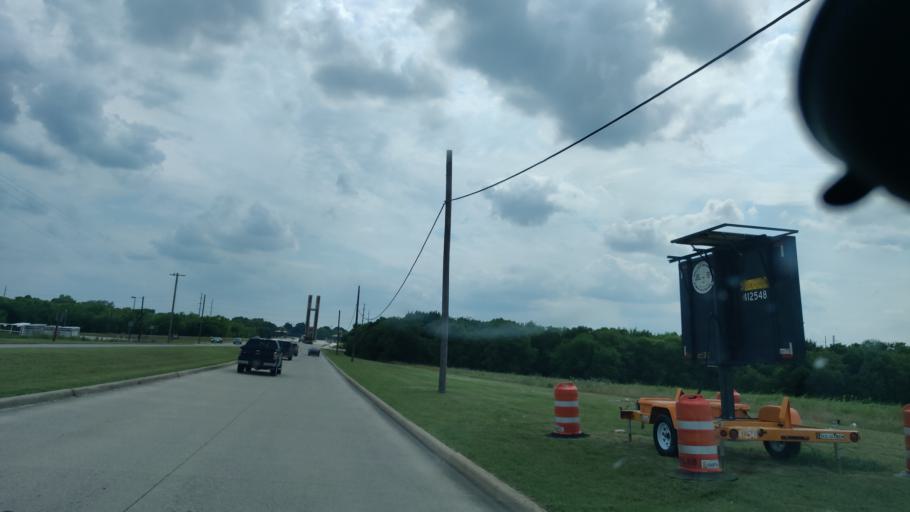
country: US
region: Texas
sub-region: Dallas County
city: Sachse
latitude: 32.9488
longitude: -96.5870
